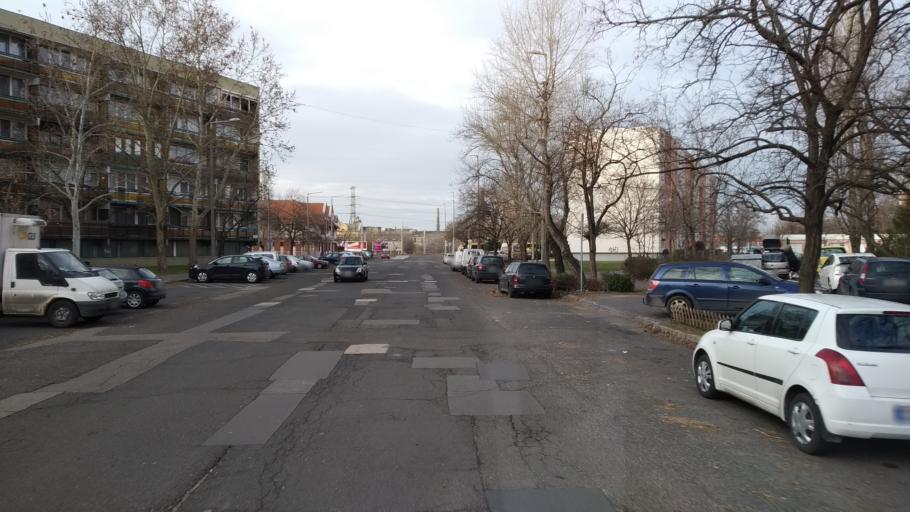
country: HU
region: Budapest
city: Budapest XX. keruelet
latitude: 47.4421
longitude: 19.0975
